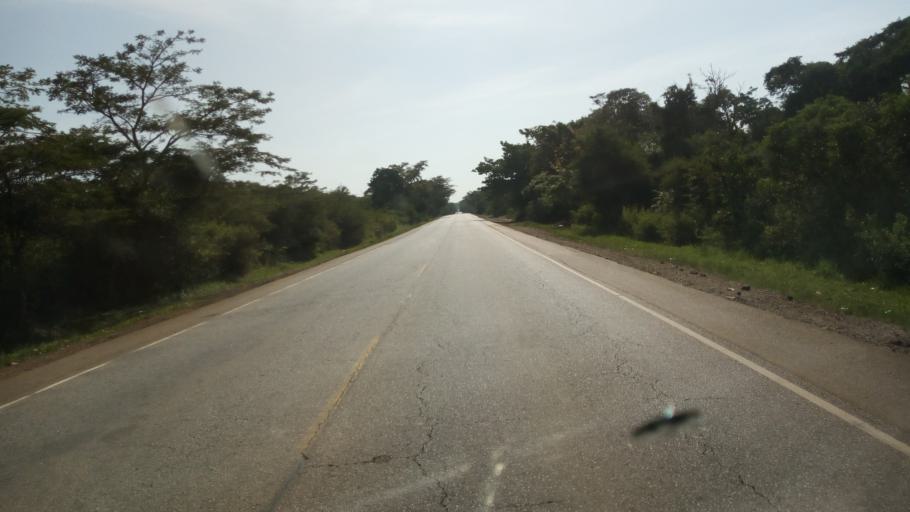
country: UG
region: Eastern Region
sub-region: Busia District
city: Busia
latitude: 0.5283
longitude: 33.9770
